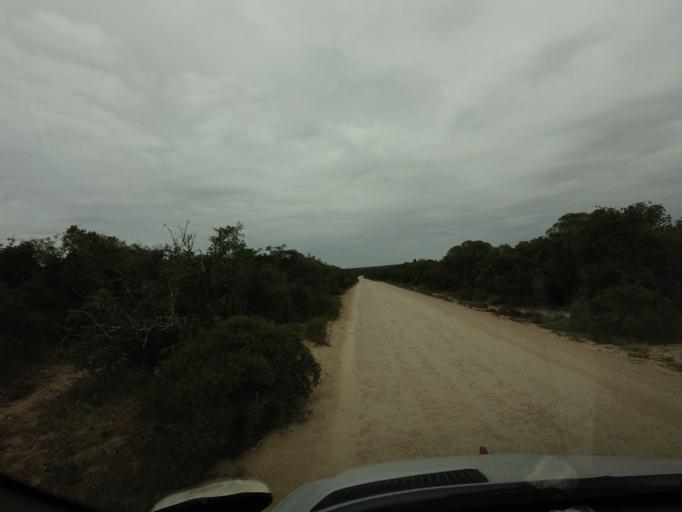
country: ZA
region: Eastern Cape
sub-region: Cacadu District Municipality
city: Kirkwood
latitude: -33.4823
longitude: 25.7748
